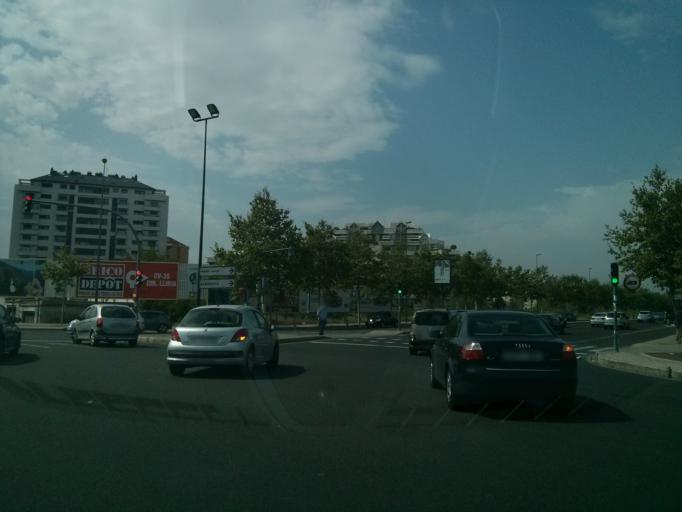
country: ES
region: Valencia
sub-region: Provincia de Valencia
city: Alboraya
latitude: 39.4821
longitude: -0.3511
